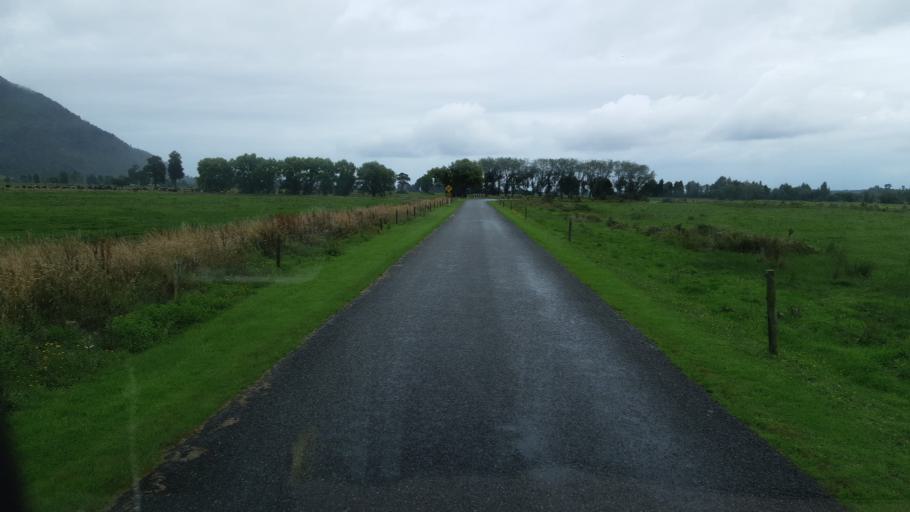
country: NZ
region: West Coast
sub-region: Westland District
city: Hokitika
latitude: -42.8833
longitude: 171.0316
